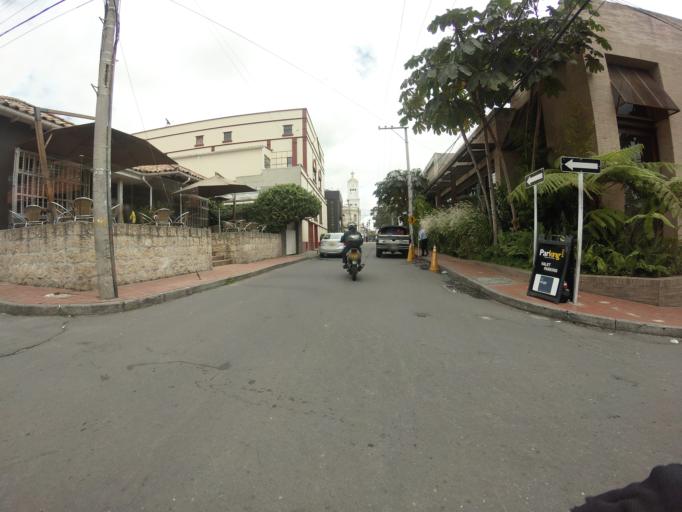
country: CO
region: Bogota D.C.
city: Barrio San Luis
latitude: 4.6961
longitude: -74.0301
